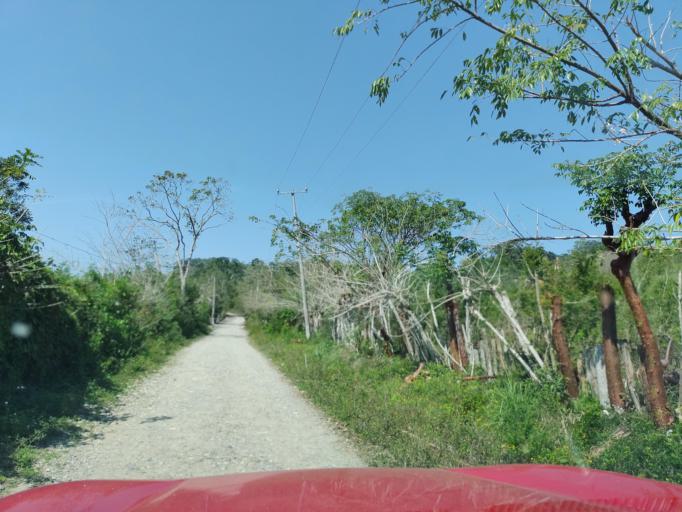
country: MX
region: Veracruz
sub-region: Papantla
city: Polutla
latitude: 20.5013
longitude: -97.2157
